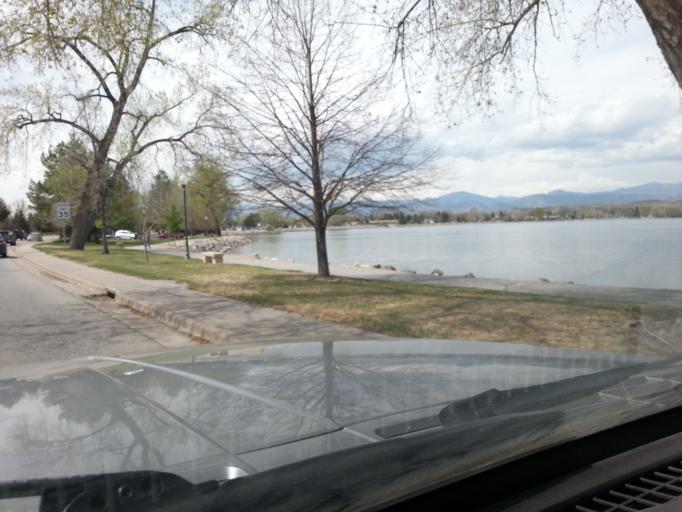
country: US
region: Colorado
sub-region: Larimer County
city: Loveland
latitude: 40.4061
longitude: -105.0824
